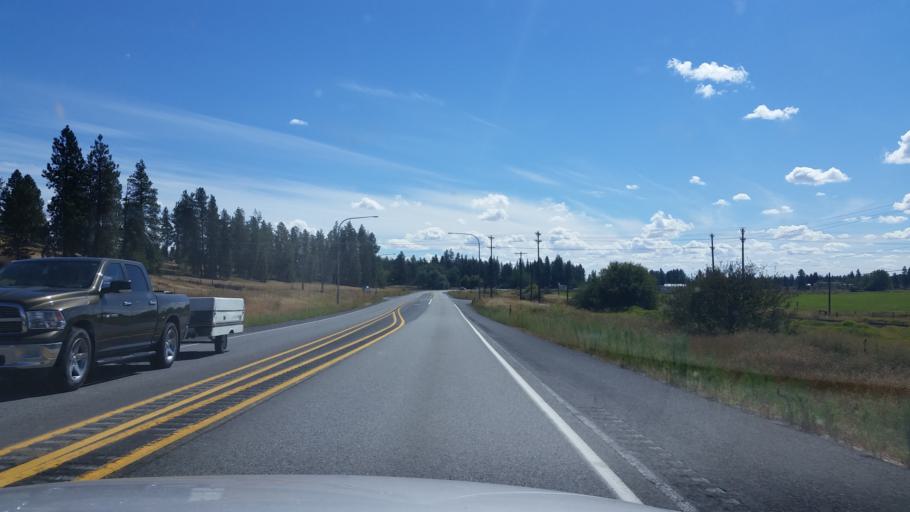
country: US
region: Washington
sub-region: Spokane County
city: Cheney
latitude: 47.5305
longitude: -117.5703
